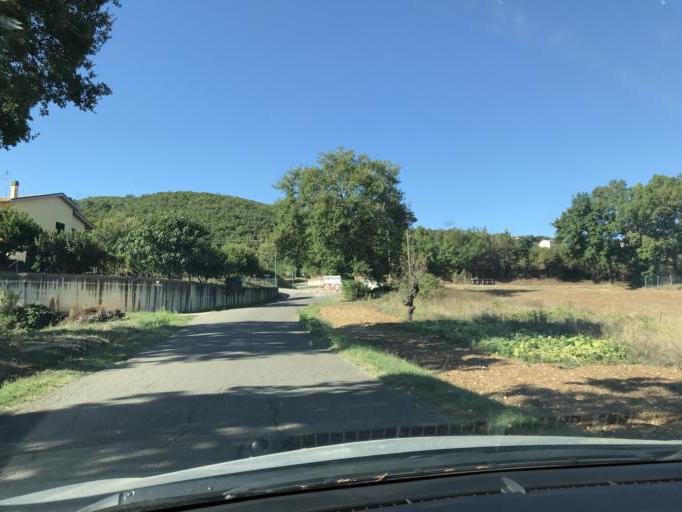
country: IT
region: Umbria
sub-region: Provincia di Terni
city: Avigliano Umbro
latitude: 42.6282
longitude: 12.4027
